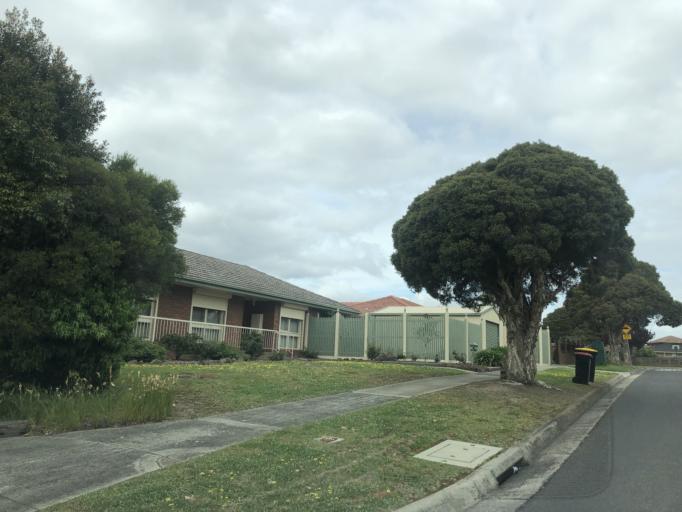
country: AU
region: Victoria
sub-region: Greater Dandenong
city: Noble Park North
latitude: -37.9472
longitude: 145.2108
